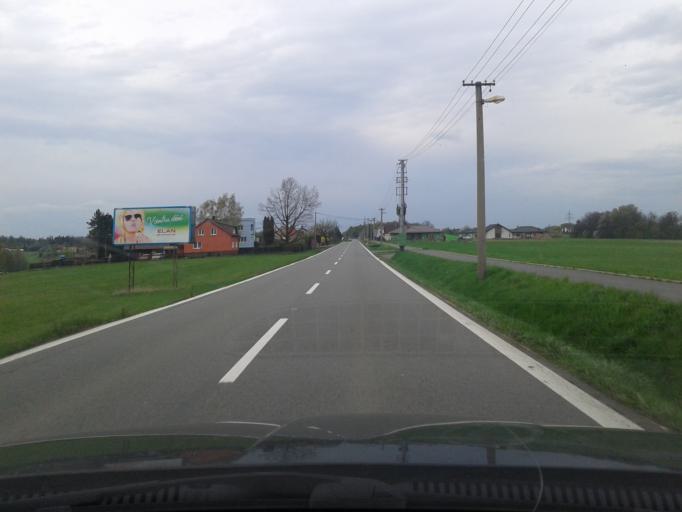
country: CZ
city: Sedliste
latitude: 49.7242
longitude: 18.3673
